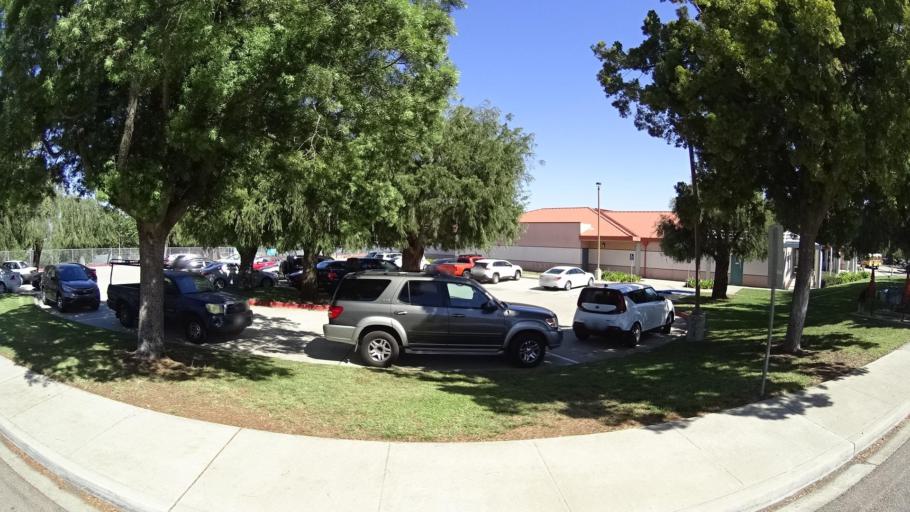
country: US
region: California
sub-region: San Diego County
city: Bonita
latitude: 32.6450
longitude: -117.0457
